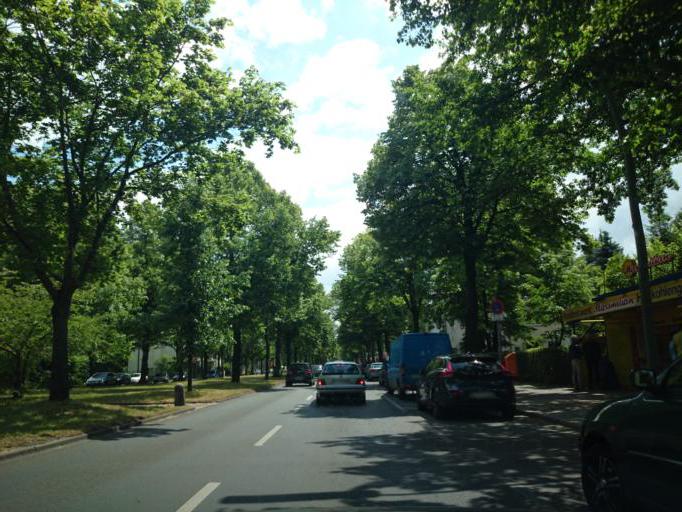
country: DE
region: Berlin
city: Lichtenrade
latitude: 52.4134
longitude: 13.4016
